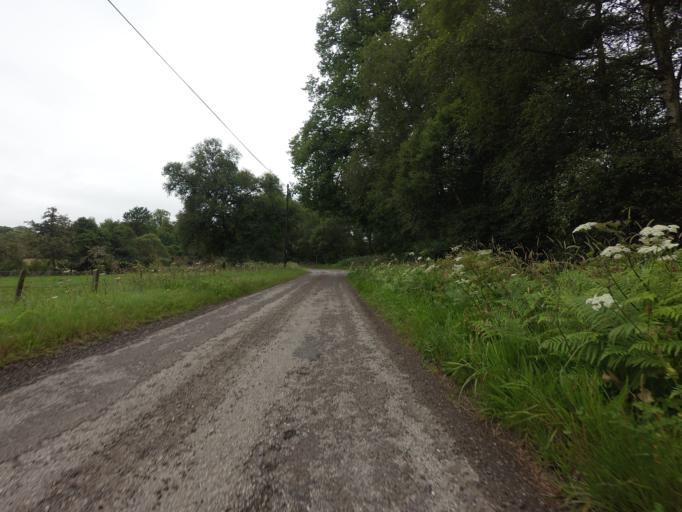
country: GB
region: Scotland
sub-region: Highland
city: Evanton
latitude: 57.9852
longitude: -4.4182
